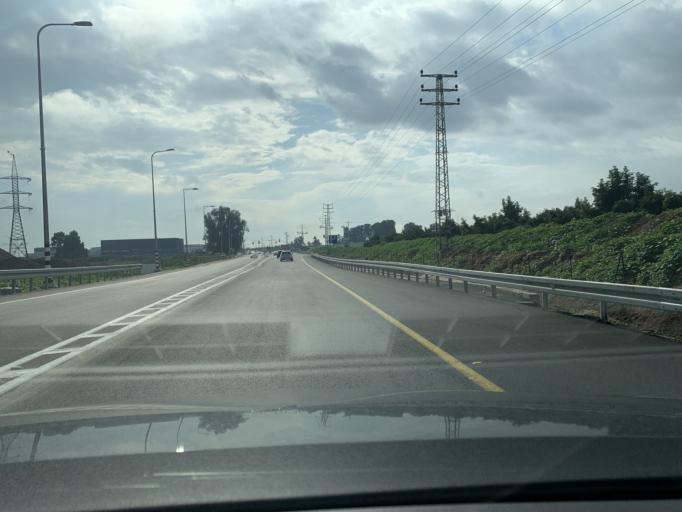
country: PS
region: West Bank
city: Qalqilyah
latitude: 32.1951
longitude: 34.9546
